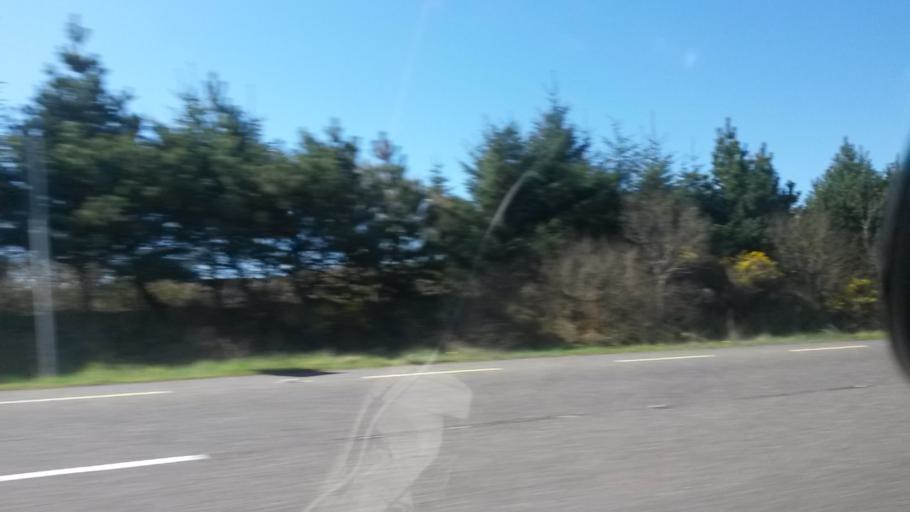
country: IE
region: Munster
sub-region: County Cork
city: Millstreet
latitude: 51.9608
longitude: -9.2374
